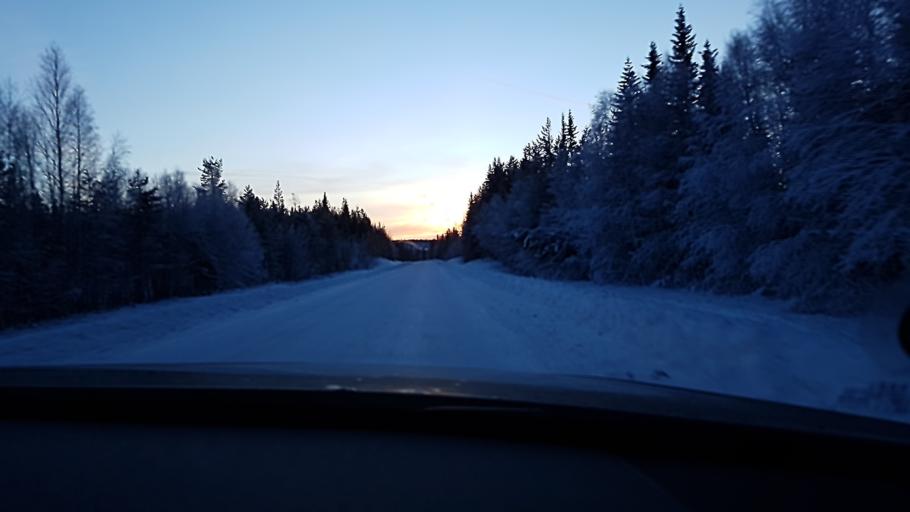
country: SE
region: Vaesterbotten
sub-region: Storumans Kommun
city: Storuman
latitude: 65.1195
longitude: 17.2211
